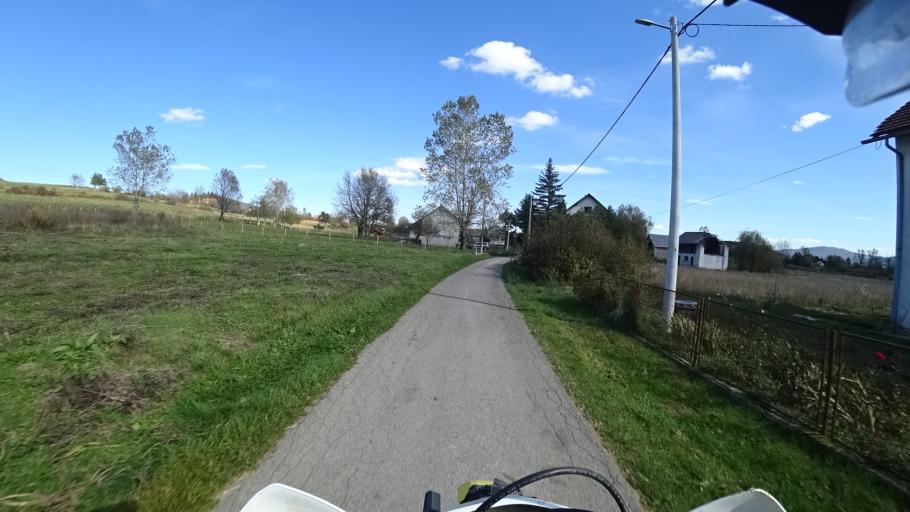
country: HR
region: Karlovacka
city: Plaski
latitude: 45.0871
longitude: 15.3607
